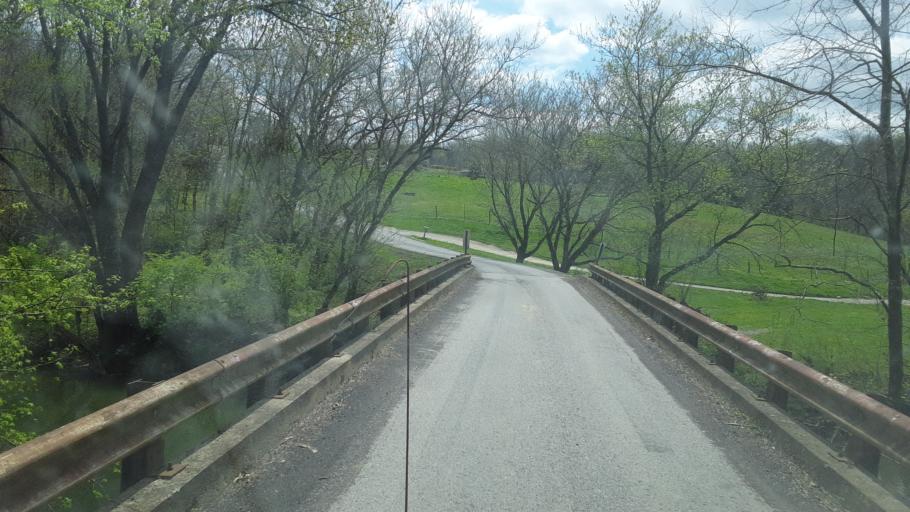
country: US
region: Kentucky
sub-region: Owen County
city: Owenton
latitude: 38.6750
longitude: -84.7986
